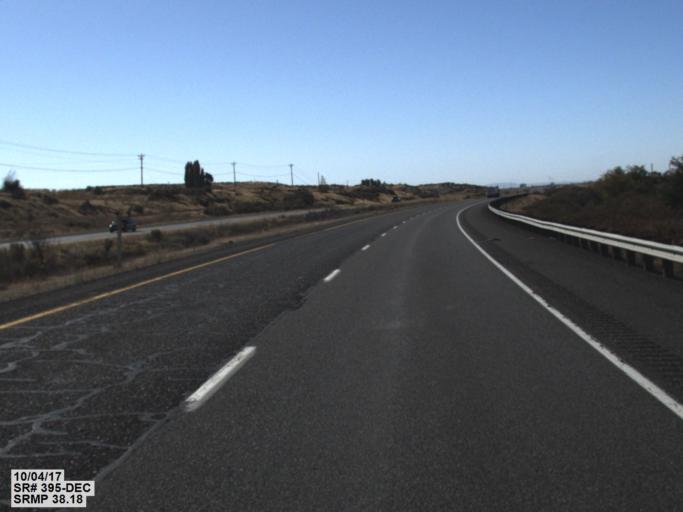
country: US
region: Washington
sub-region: Franklin County
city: Basin City
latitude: 46.4596
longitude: -119.0135
